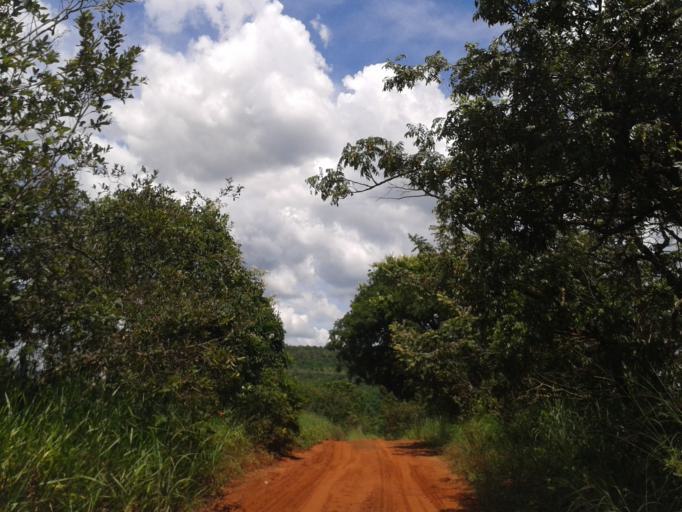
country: BR
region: Minas Gerais
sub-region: Ituiutaba
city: Ituiutaba
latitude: -18.8483
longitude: -49.5035
